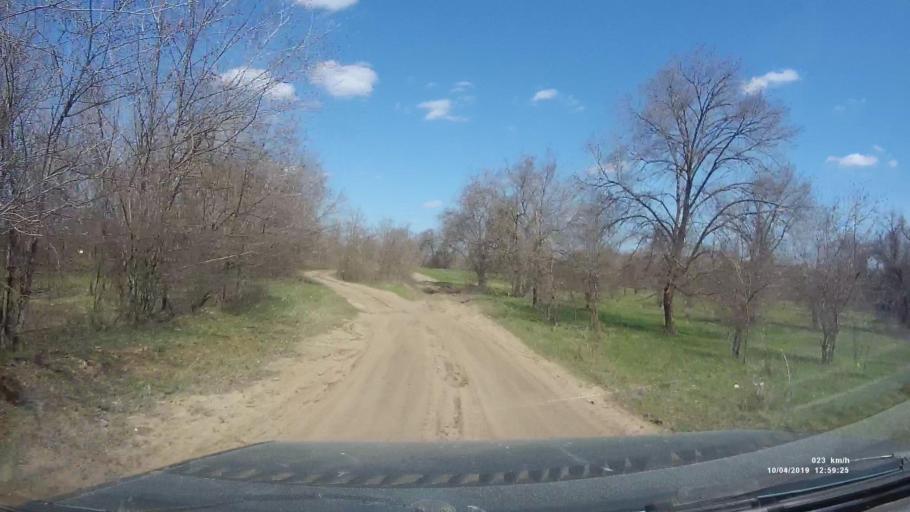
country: RU
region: Rostov
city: Masalovka
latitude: 48.3776
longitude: 40.2279
